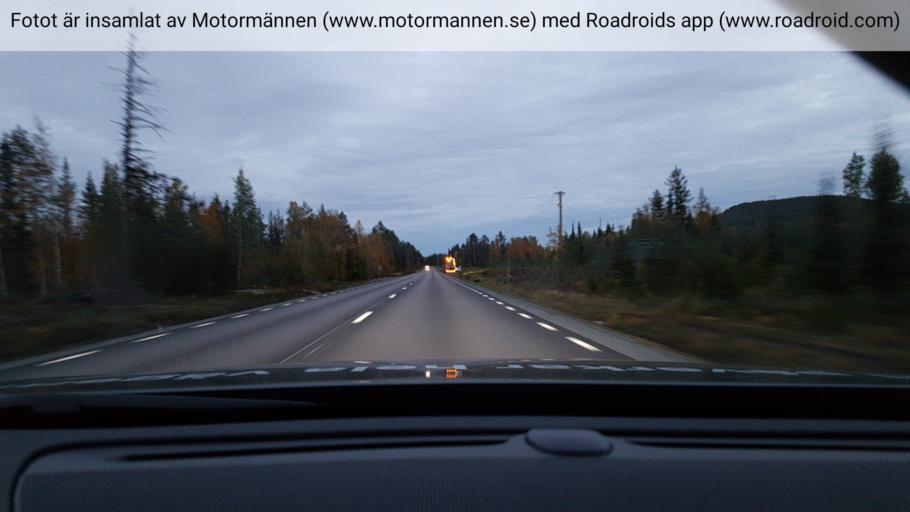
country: SE
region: Norrbotten
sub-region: Alvsbyns Kommun
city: AElvsbyn
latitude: 65.7528
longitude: 20.9026
